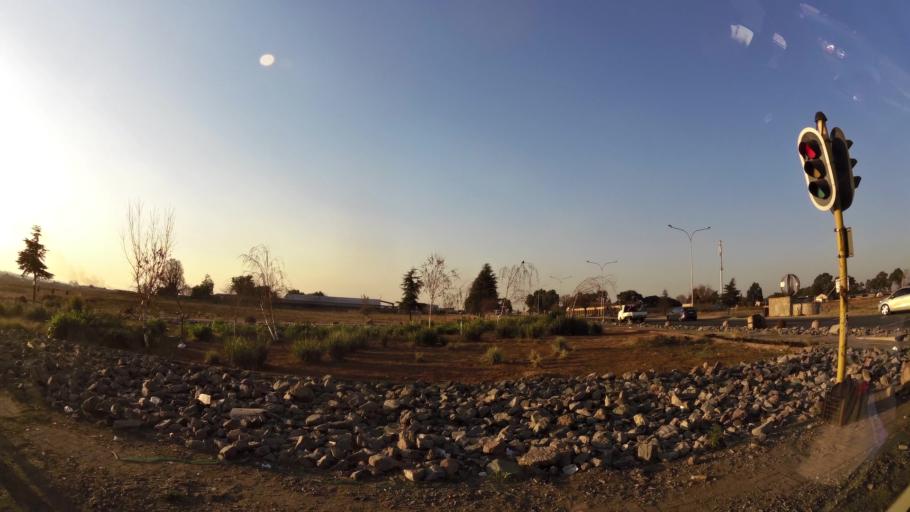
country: ZA
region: Gauteng
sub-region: West Rand District Municipality
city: Randfontein
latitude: -26.2078
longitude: 27.6943
